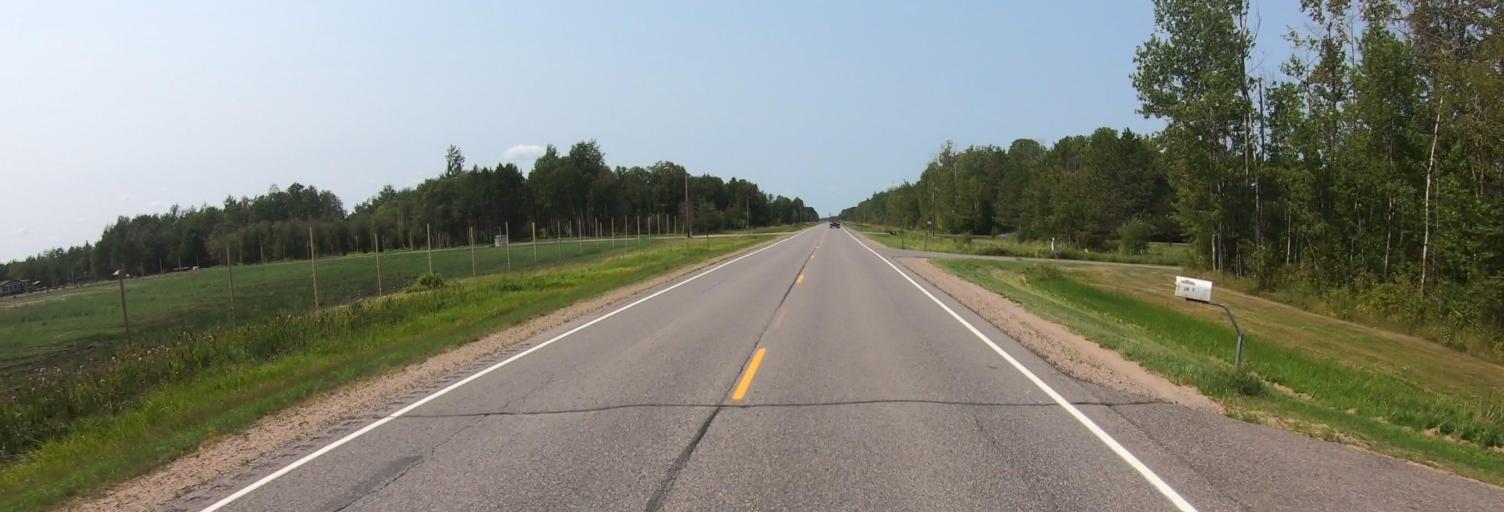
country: US
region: Minnesota
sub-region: Koochiching County
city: International Falls
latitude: 48.5189
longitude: -93.6037
